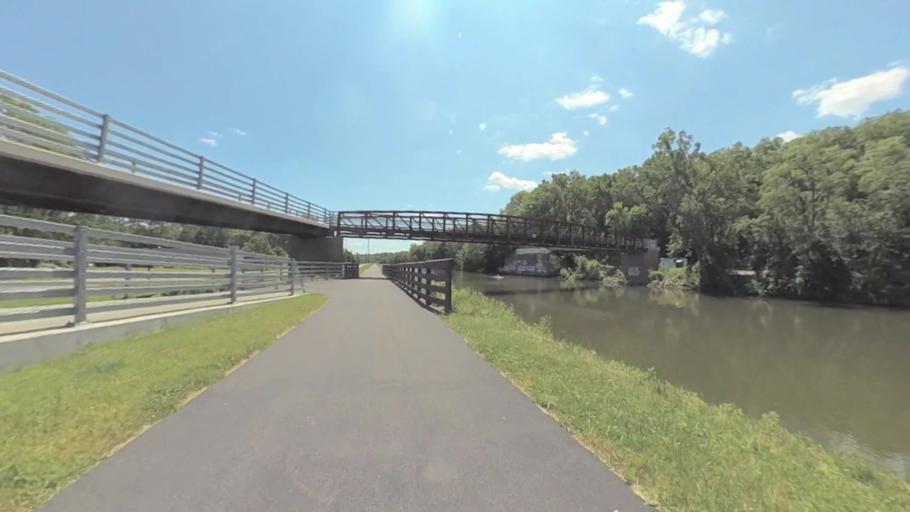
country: US
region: New York
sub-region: Monroe County
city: Fairport
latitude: 43.0952
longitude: -77.4292
